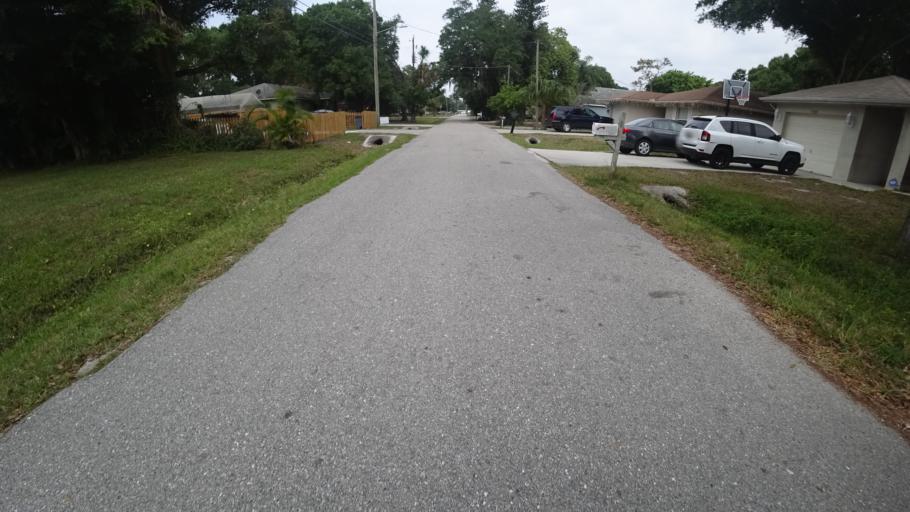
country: US
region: Florida
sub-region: Manatee County
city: Samoset
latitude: 27.4723
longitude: -82.5431
